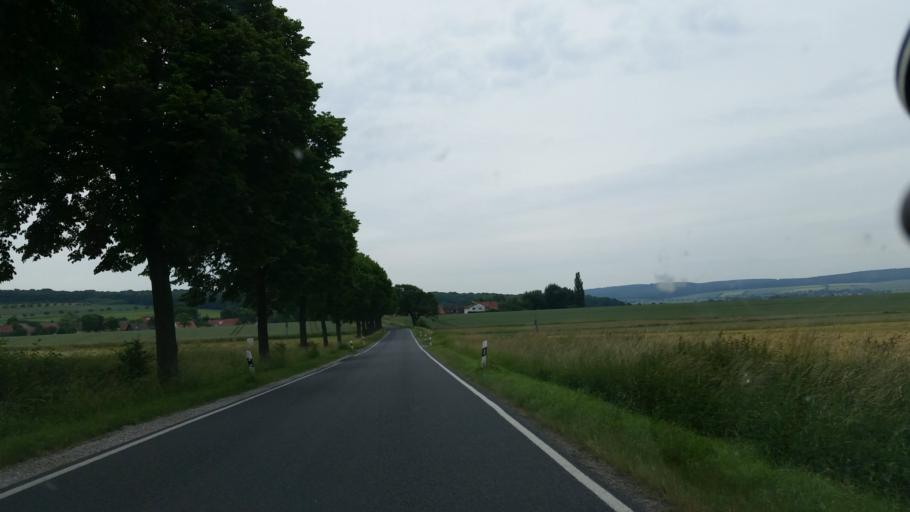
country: DE
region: Lower Saxony
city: Erkerode
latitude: 52.2918
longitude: 10.7424
